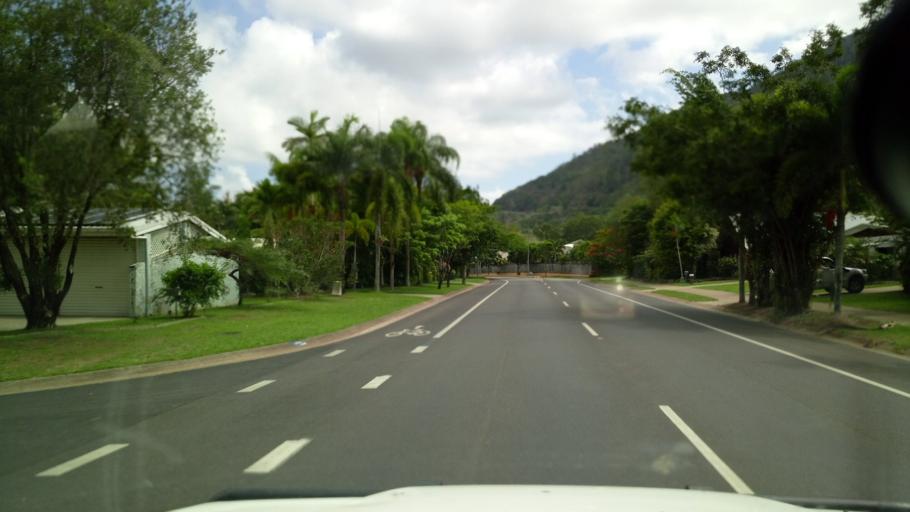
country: AU
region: Queensland
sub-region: Cairns
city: Redlynch
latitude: -16.9167
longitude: 145.7211
